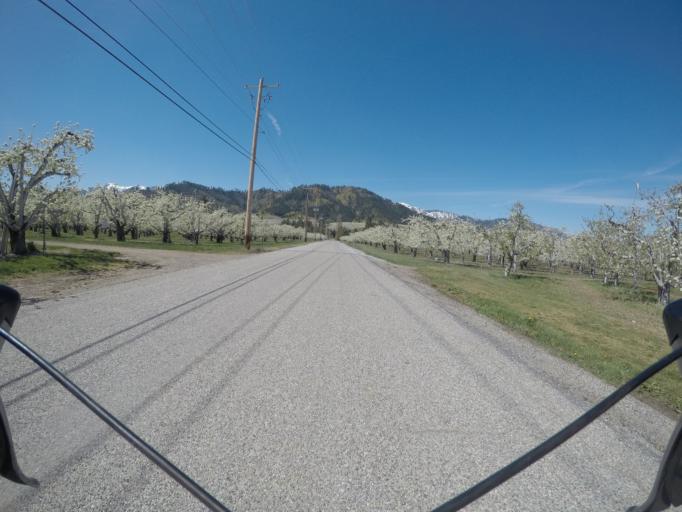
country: US
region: Washington
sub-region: Chelan County
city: Leavenworth
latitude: 47.5642
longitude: -120.5942
